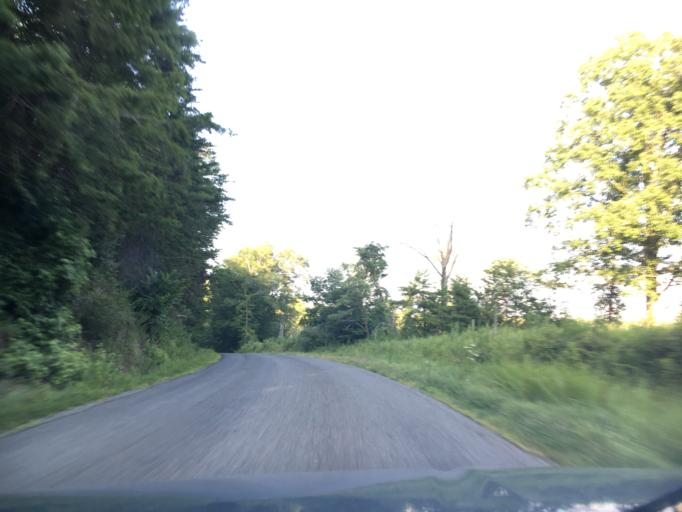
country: US
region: Virginia
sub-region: Halifax County
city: Mountain Road
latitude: 36.8410
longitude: -79.1691
